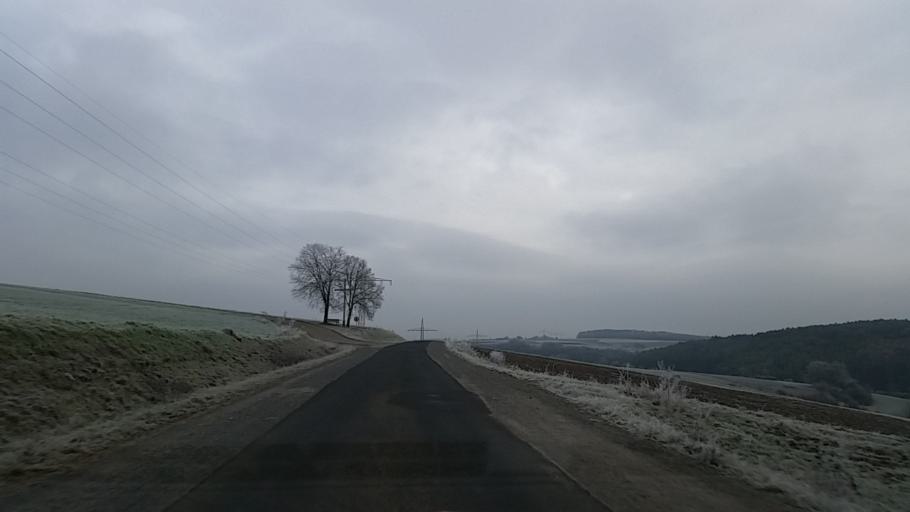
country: DE
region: Bavaria
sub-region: Regierungsbezirk Unterfranken
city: Fuchsstadt
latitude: 50.0336
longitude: 9.8993
